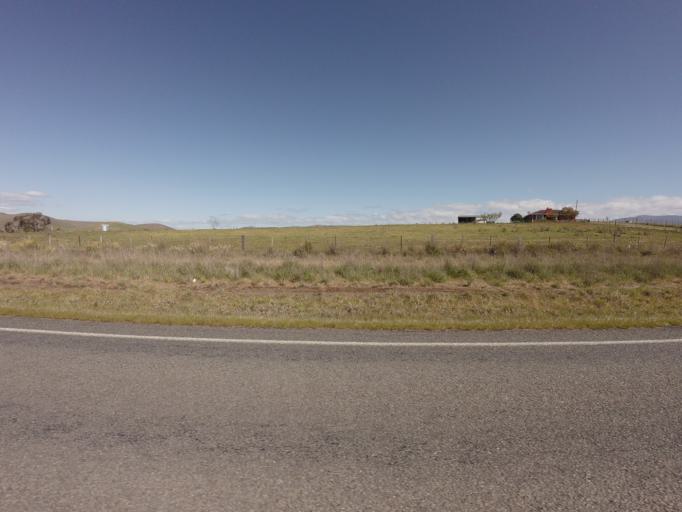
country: AU
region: Tasmania
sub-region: Derwent Valley
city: New Norfolk
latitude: -42.5528
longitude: 146.8017
